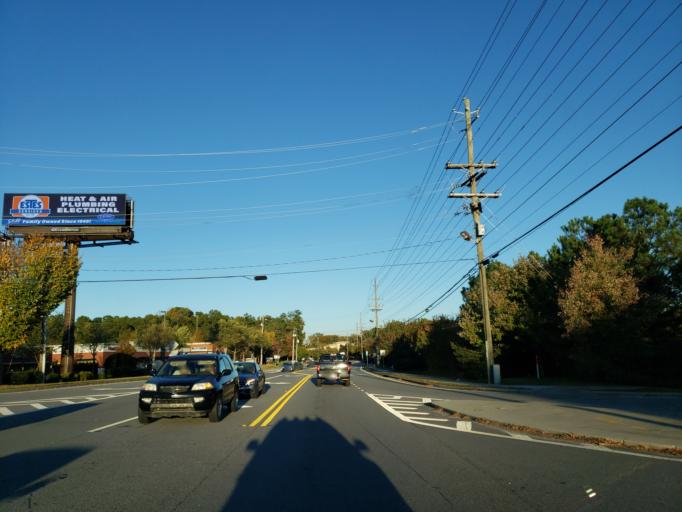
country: US
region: Georgia
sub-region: Fulton County
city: Alpharetta
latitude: 34.0950
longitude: -84.2771
